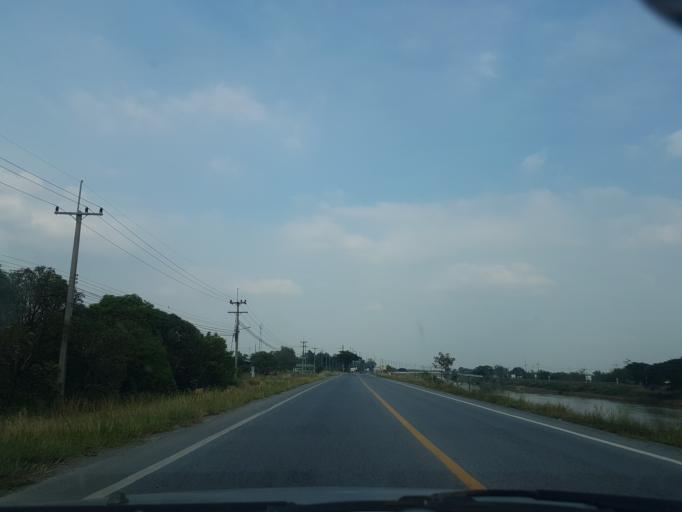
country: TH
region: Phra Nakhon Si Ayutthaya
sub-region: Amphoe Tha Ruea
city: Tha Ruea
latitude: 14.5279
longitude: 100.7424
